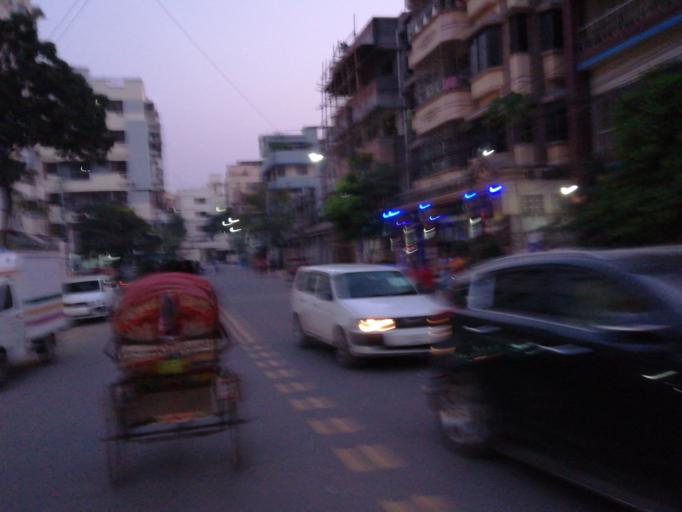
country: BD
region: Dhaka
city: Tungi
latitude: 23.8651
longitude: 90.3889
